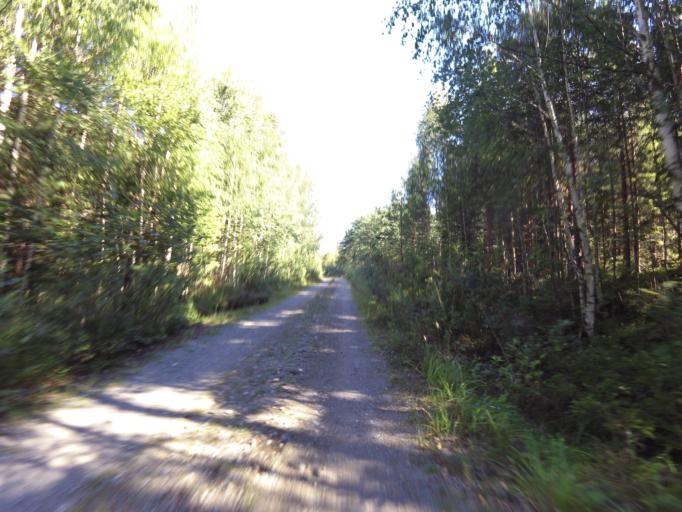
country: SE
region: Gaevleborg
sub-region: Hofors Kommun
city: Hofors
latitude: 60.5479
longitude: 16.4274
